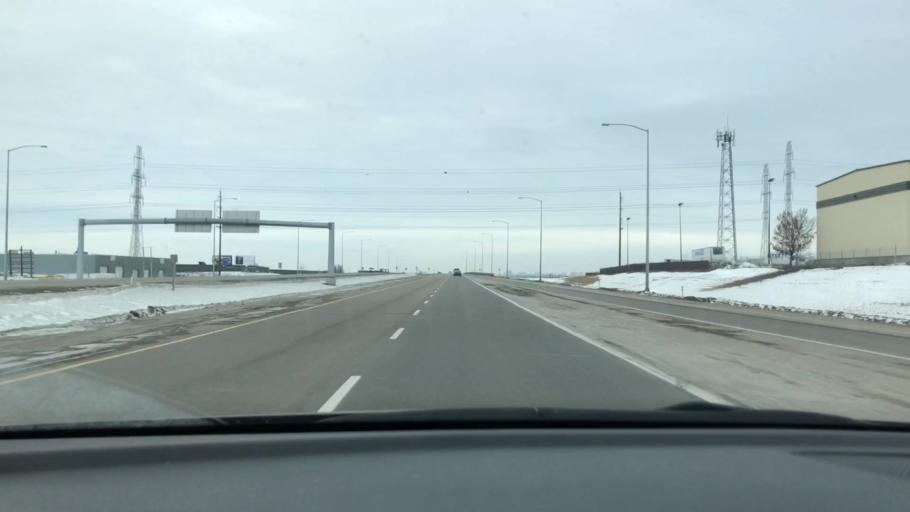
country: CA
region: Alberta
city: Sherwood Park
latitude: 53.5177
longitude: -113.3777
